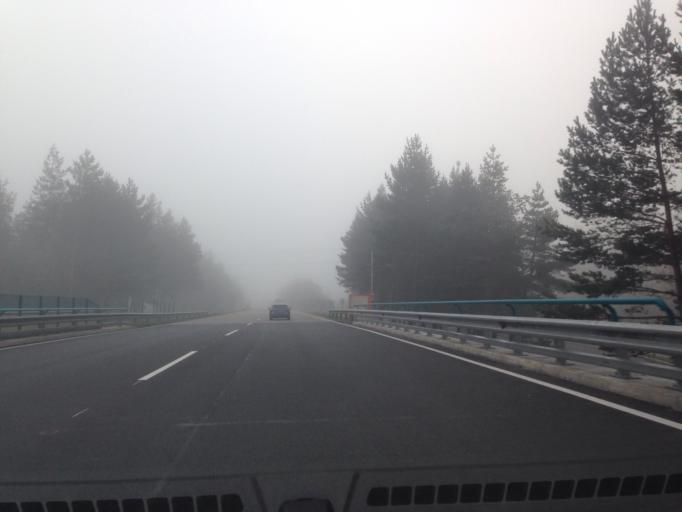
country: AT
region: Tyrol
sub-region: Politischer Bezirk Reutte
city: Lermoos
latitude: 47.4092
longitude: 10.8635
